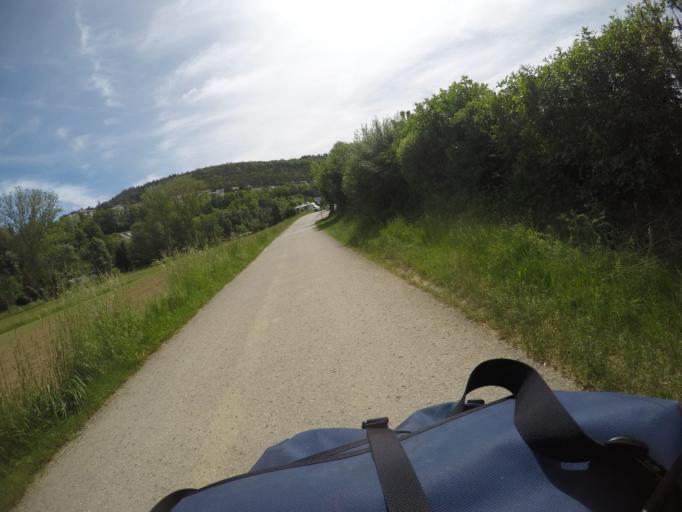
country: DE
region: Baden-Wuerttemberg
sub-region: Karlsruhe Region
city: Nagold
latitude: 48.5650
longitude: 8.7206
